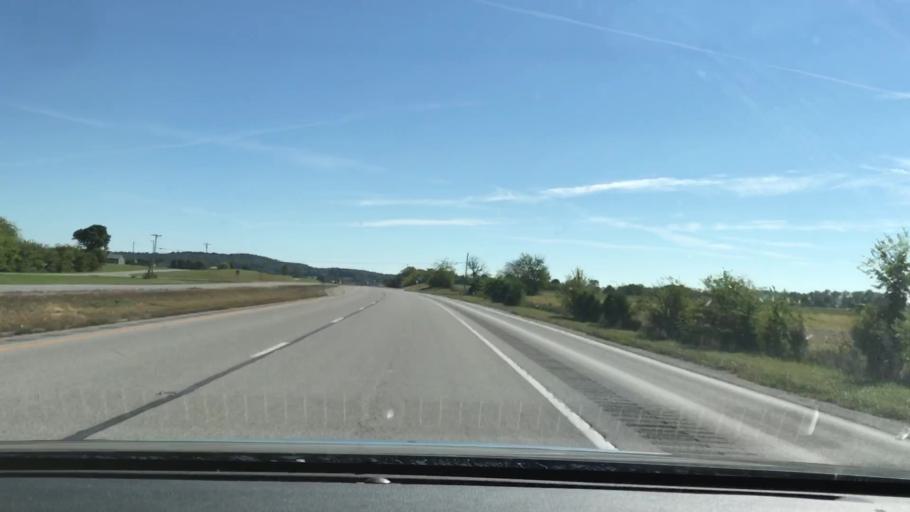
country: US
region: Kentucky
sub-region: Todd County
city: Elkton
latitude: 36.8419
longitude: -87.2629
